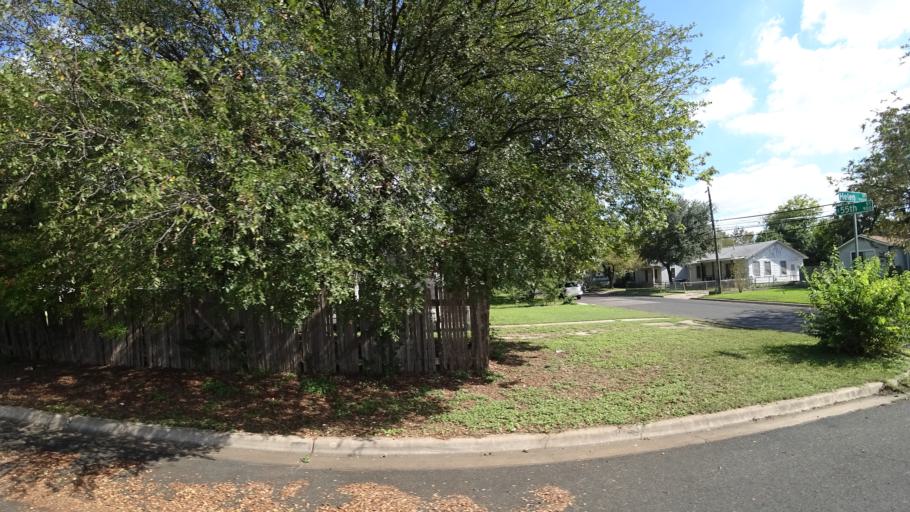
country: US
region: Texas
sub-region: Travis County
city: Austin
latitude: 30.3158
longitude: -97.7122
